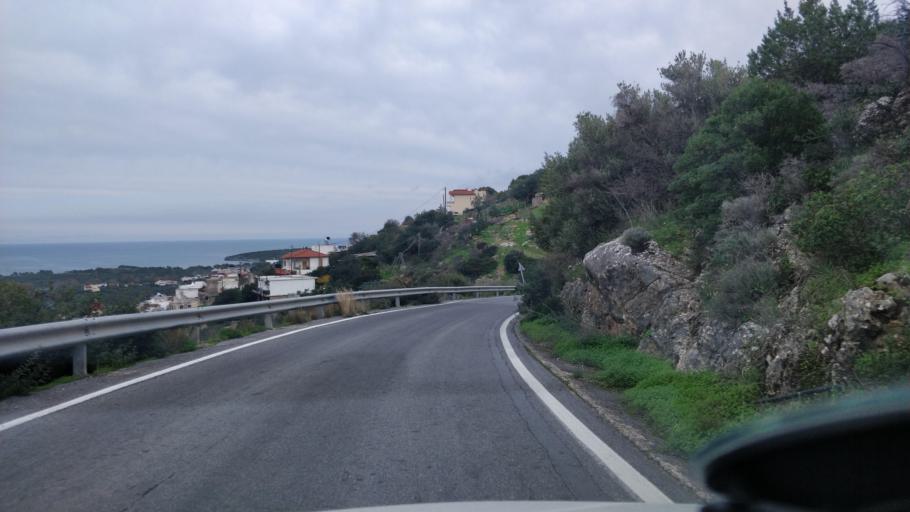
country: GR
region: Crete
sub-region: Nomos Lasithiou
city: Agios Nikolaos
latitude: 35.1127
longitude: 25.7205
